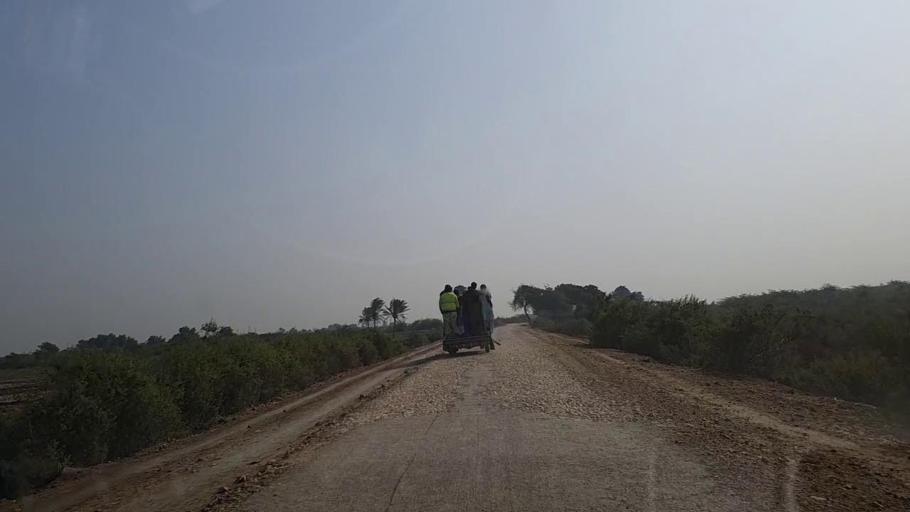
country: PK
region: Sindh
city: Keti Bandar
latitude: 24.2456
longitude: 67.6351
